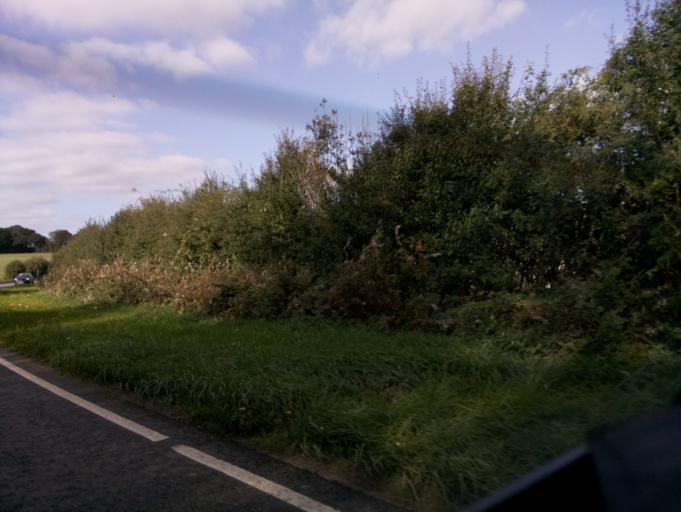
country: GB
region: England
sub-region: Hampshire
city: Four Marks
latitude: 51.1811
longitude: -1.0600
